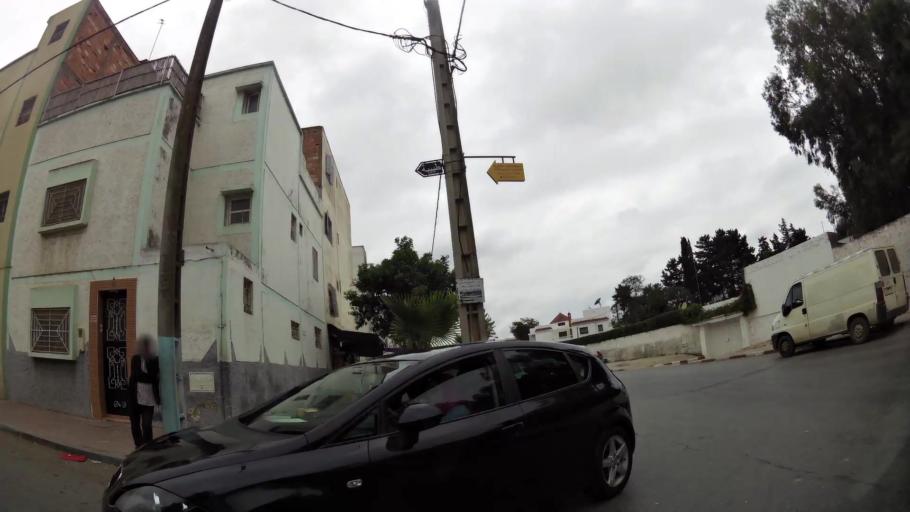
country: MA
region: Rabat-Sale-Zemmour-Zaer
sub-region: Rabat
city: Rabat
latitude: 33.9718
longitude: -6.8212
